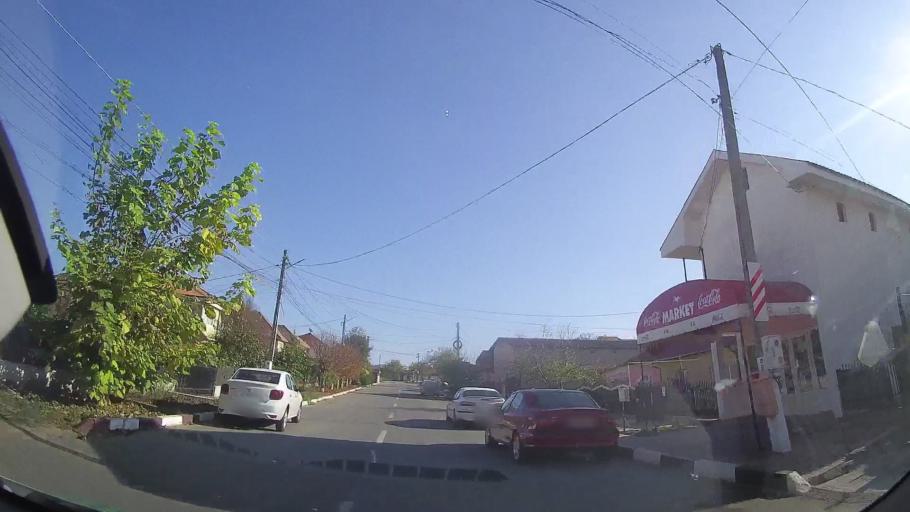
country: RO
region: Constanta
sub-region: Comuna Costinesti
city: Schitu
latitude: 43.9407
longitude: 28.6301
